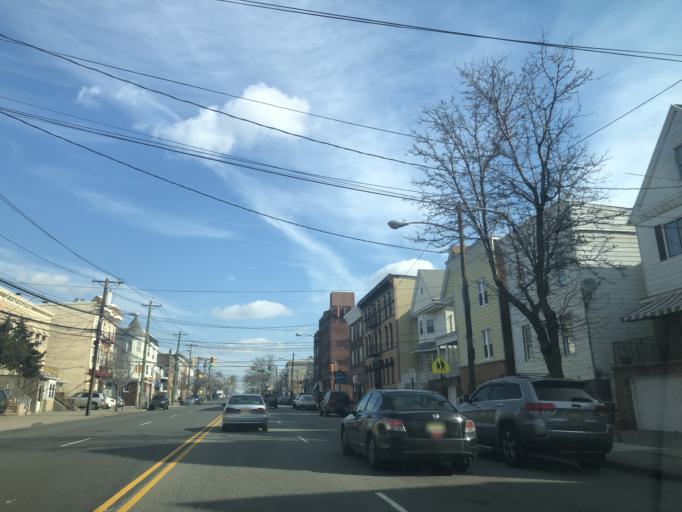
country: US
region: New Jersey
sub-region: Hudson County
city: Bayonne
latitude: 40.6680
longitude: -74.1213
